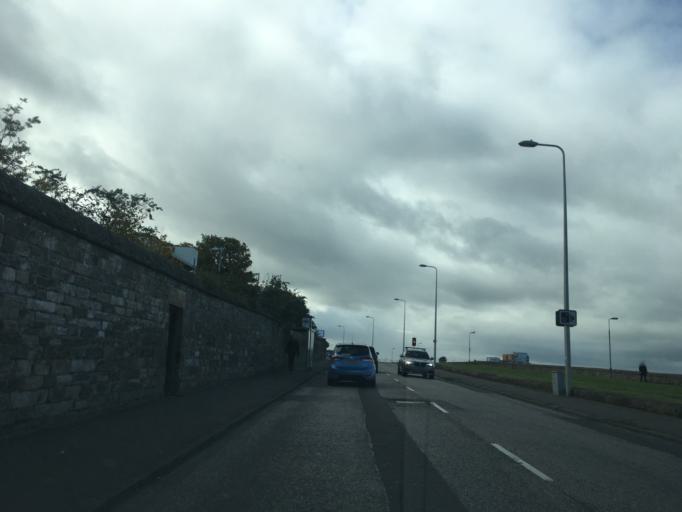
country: GB
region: Scotland
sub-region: Edinburgh
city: Edinburgh
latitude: 55.9803
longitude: -3.2109
